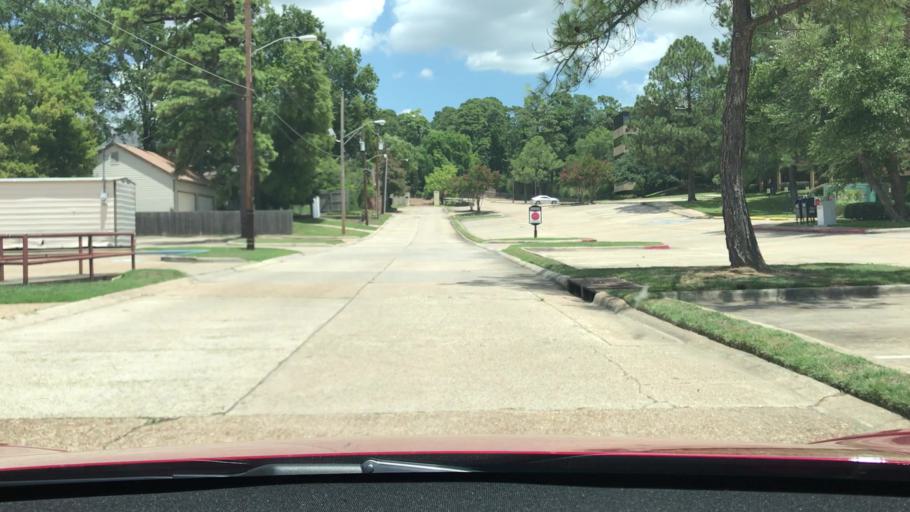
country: US
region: Louisiana
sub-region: Bossier Parish
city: Bossier City
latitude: 32.4550
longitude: -93.7494
